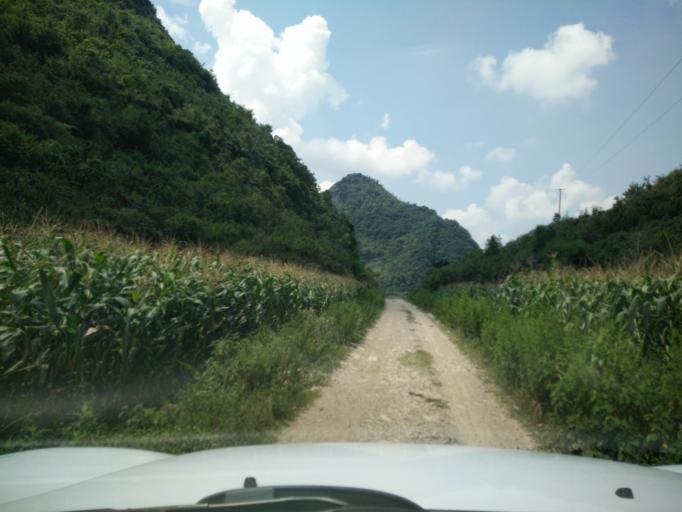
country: CN
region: Guangxi Zhuangzu Zizhiqu
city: Xinzhou
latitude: 25.0237
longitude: 105.7057
